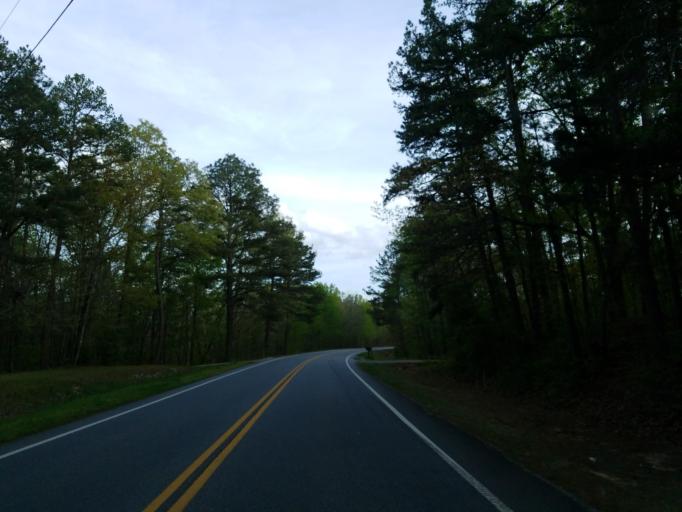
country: US
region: Georgia
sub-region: Cherokee County
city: Ball Ground
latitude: 34.3149
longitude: -84.2699
